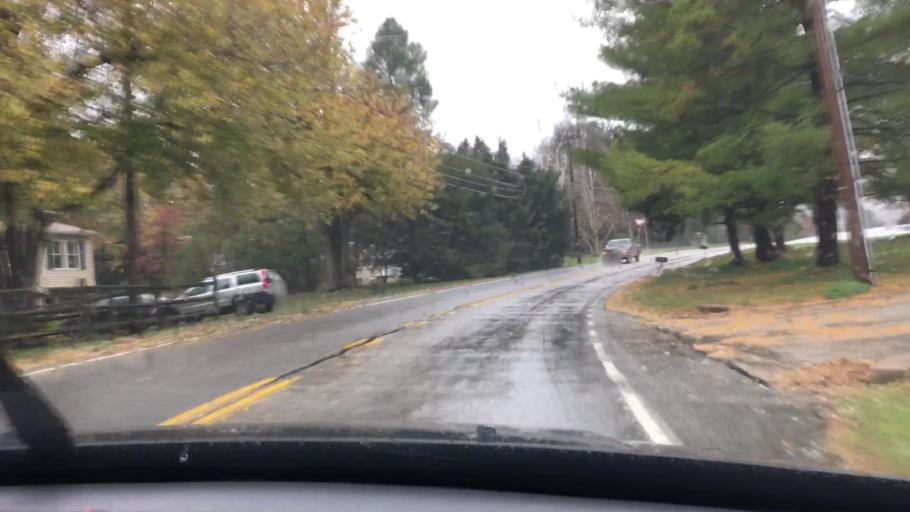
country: US
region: Pennsylvania
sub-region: York County
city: Glen Rock
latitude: 39.7675
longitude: -76.7339
